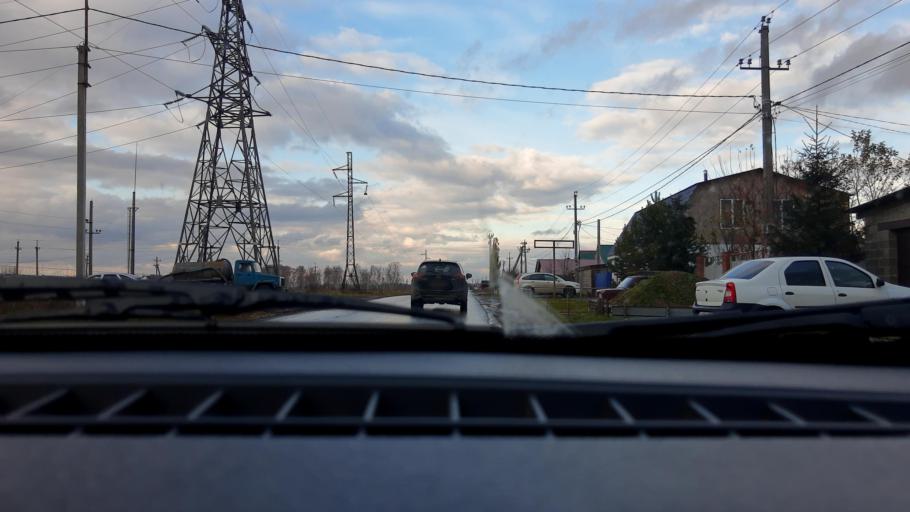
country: RU
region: Bashkortostan
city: Ufa
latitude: 54.8429
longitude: 55.9995
